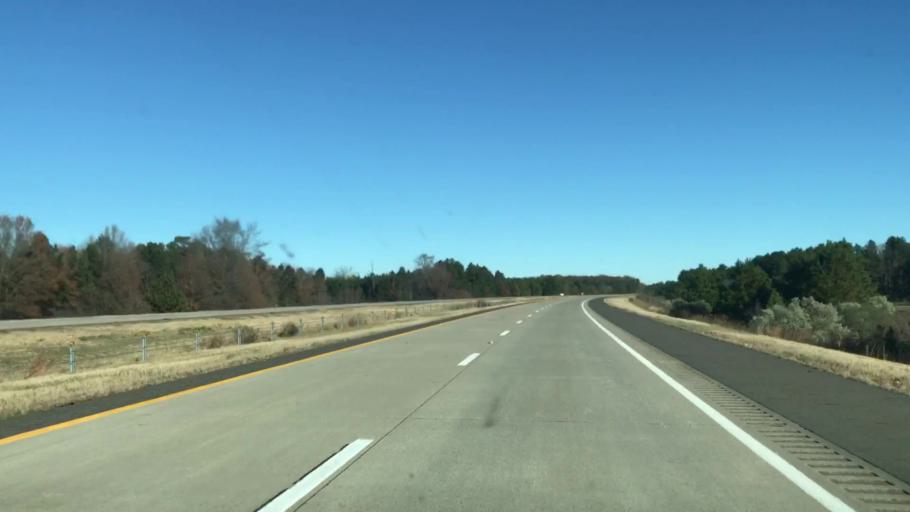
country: US
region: Texas
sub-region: Cass County
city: Queen City
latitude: 33.1995
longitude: -93.8772
